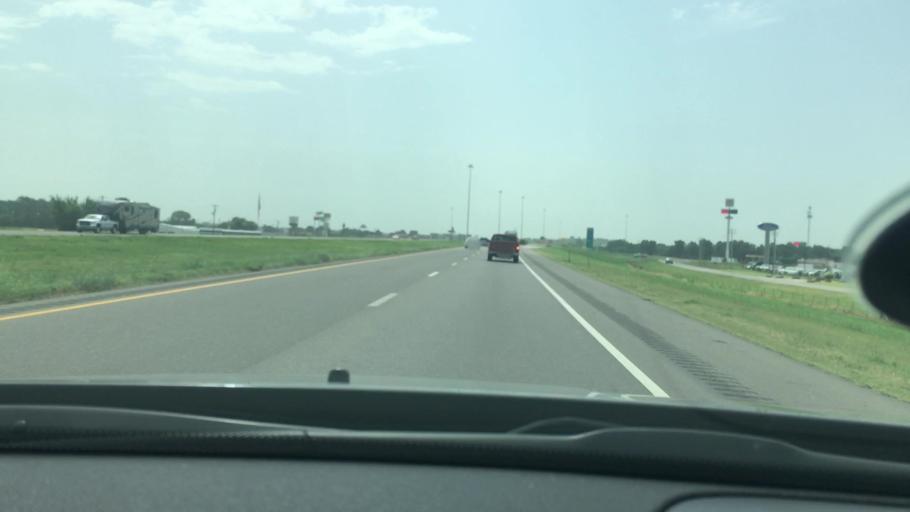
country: US
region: Oklahoma
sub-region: Garvin County
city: Pauls Valley
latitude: 34.7451
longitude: -97.2687
